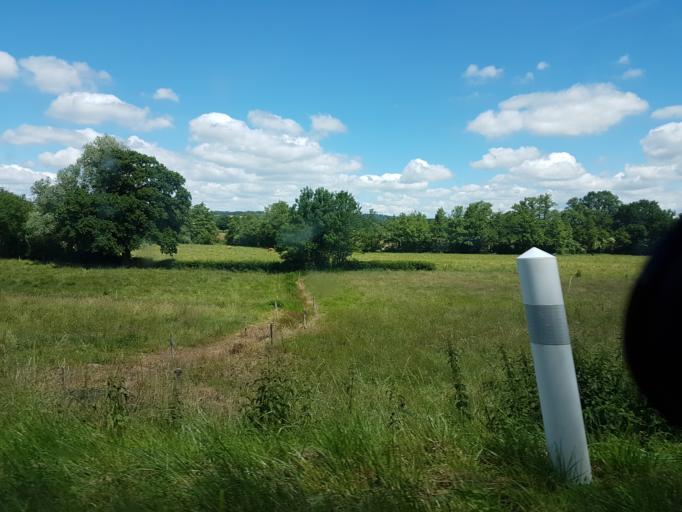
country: FR
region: Bourgogne
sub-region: Departement de Saone-et-Loire
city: Curgy
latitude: 47.0286
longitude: 4.4282
